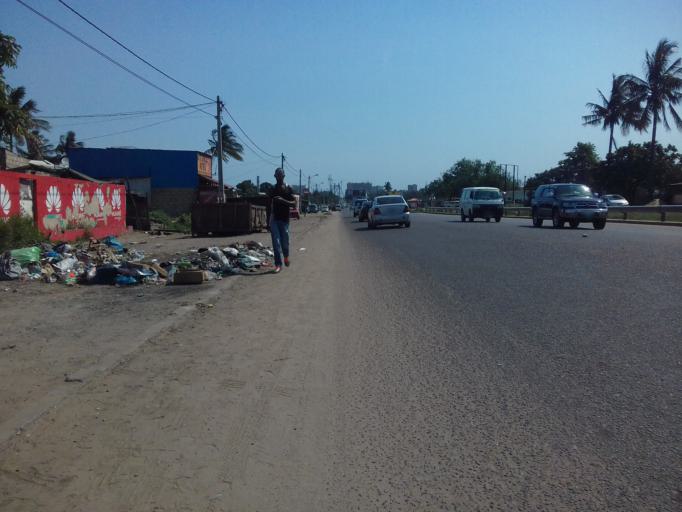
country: MZ
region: Maputo City
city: Maputo
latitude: -25.9447
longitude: 32.5728
